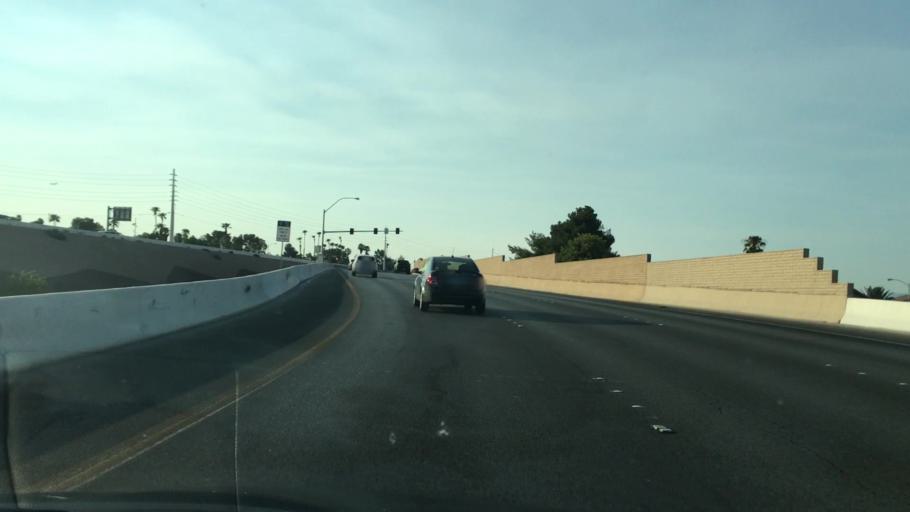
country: US
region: Nevada
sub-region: Clark County
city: Whitney
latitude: 36.1011
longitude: -115.0808
